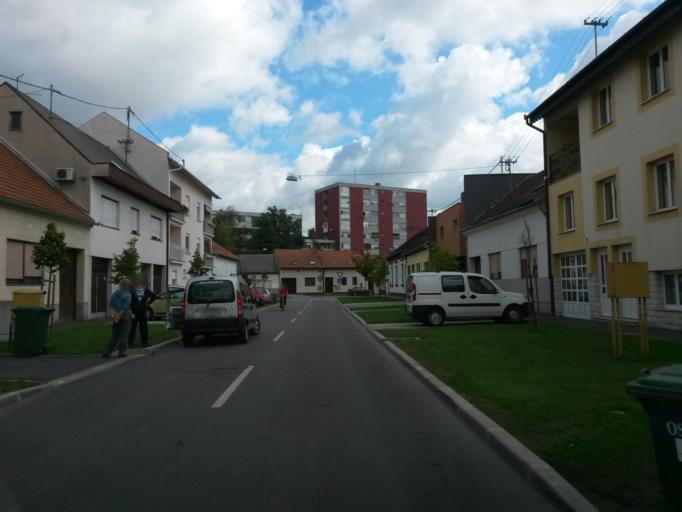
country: HR
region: Osjecko-Baranjska
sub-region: Grad Osijek
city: Osijek
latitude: 45.5558
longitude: 18.6682
